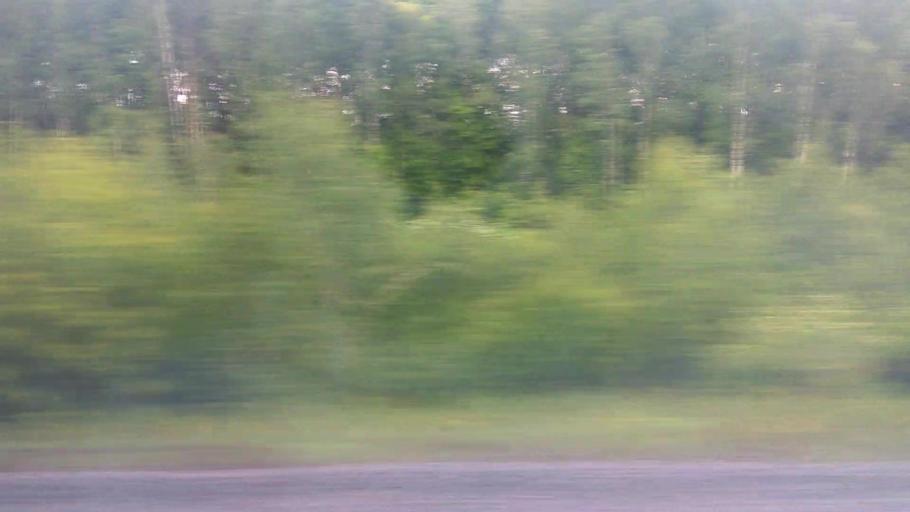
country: RU
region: Moskovskaya
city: Mikhnevo
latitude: 55.0799
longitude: 37.9759
